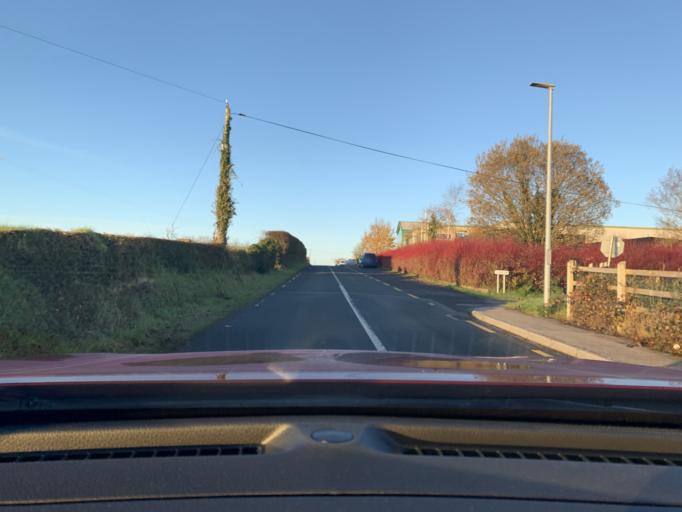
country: IE
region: Connaught
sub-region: Sligo
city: Ballymote
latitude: 54.0867
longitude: -8.5321
